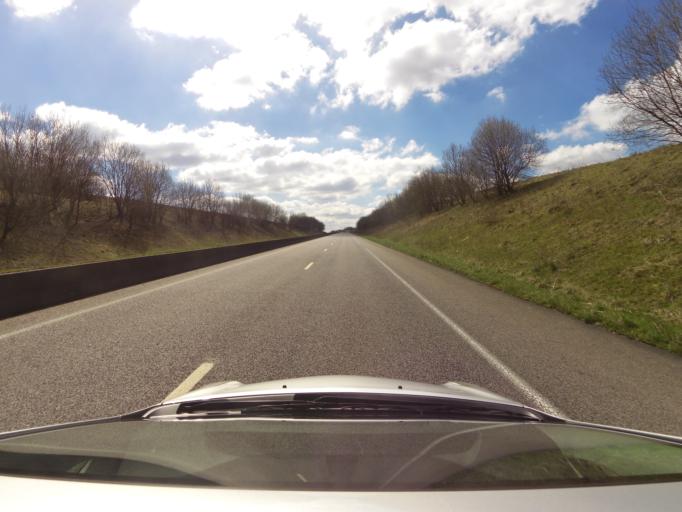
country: FR
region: Haute-Normandie
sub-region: Departement de la Seine-Maritime
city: Foucarmont
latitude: 49.8568
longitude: 1.5536
